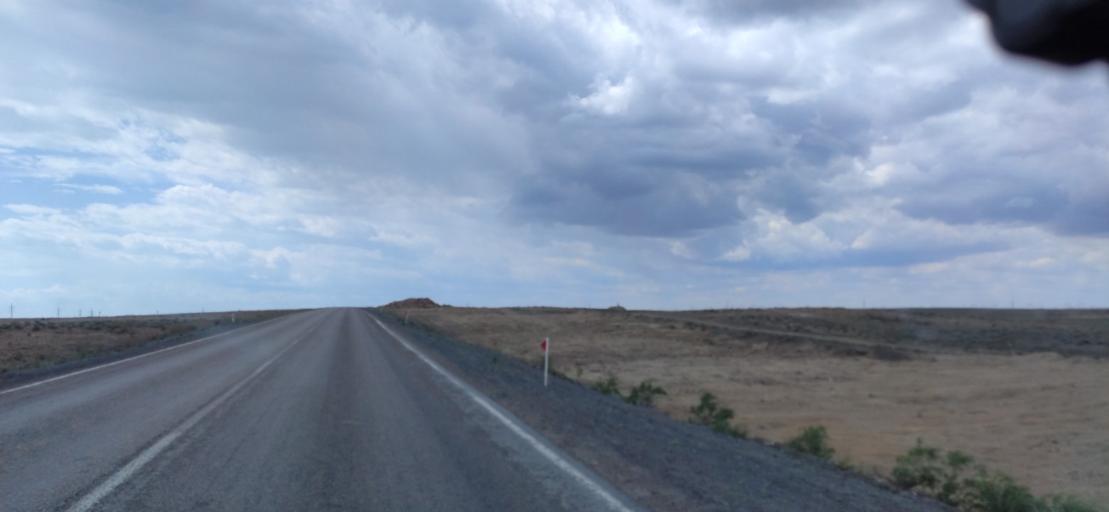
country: KZ
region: Qaraghandy
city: Saryshaghan
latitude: 46.0765
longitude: 73.6034
